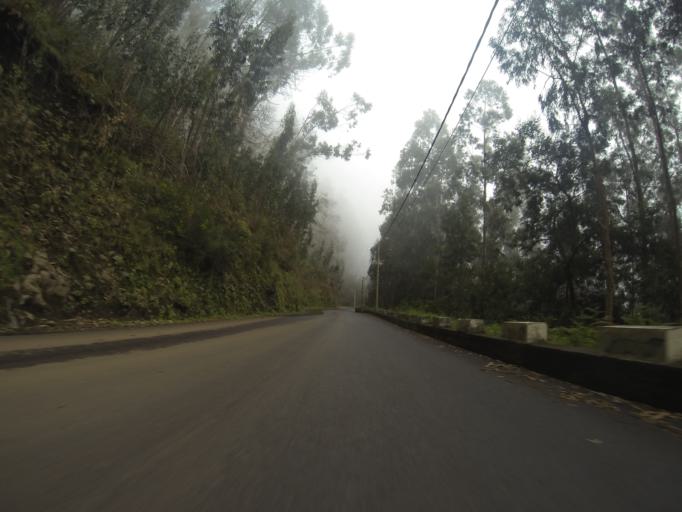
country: PT
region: Madeira
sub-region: Camara de Lobos
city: Curral das Freiras
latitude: 32.6975
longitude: -16.9537
